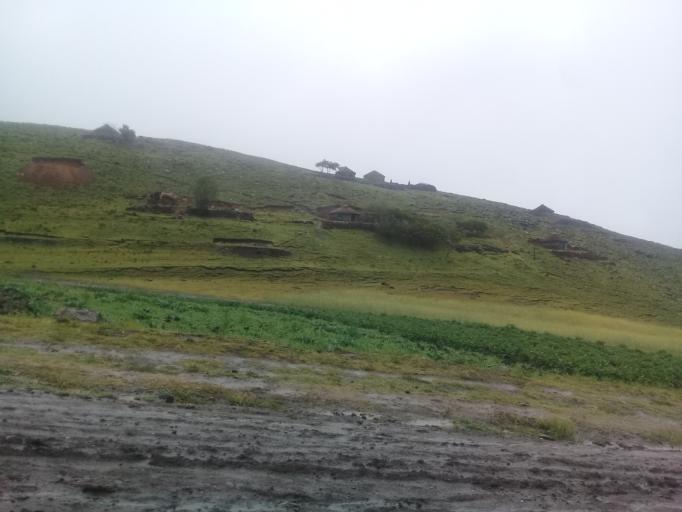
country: LS
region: Mokhotlong
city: Mokhotlong
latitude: -29.3870
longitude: 28.9779
